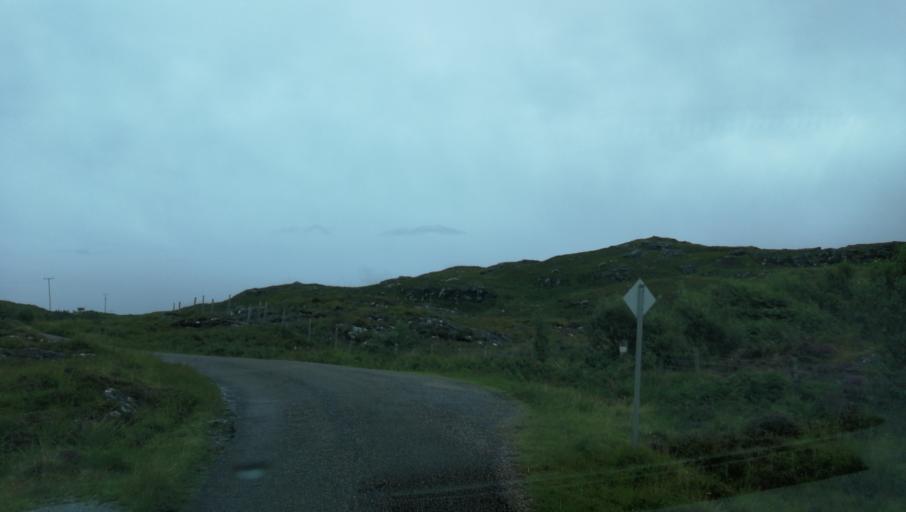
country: GB
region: Scotland
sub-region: Argyll and Bute
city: Isle Of Mull
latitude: 56.7234
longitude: -6.1853
